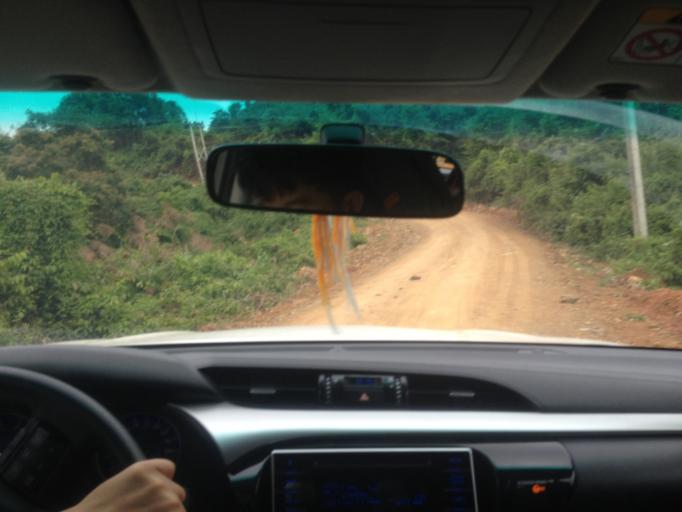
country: TH
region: Nan
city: Chaloem Phra Kiat
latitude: 19.9716
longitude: 101.1362
